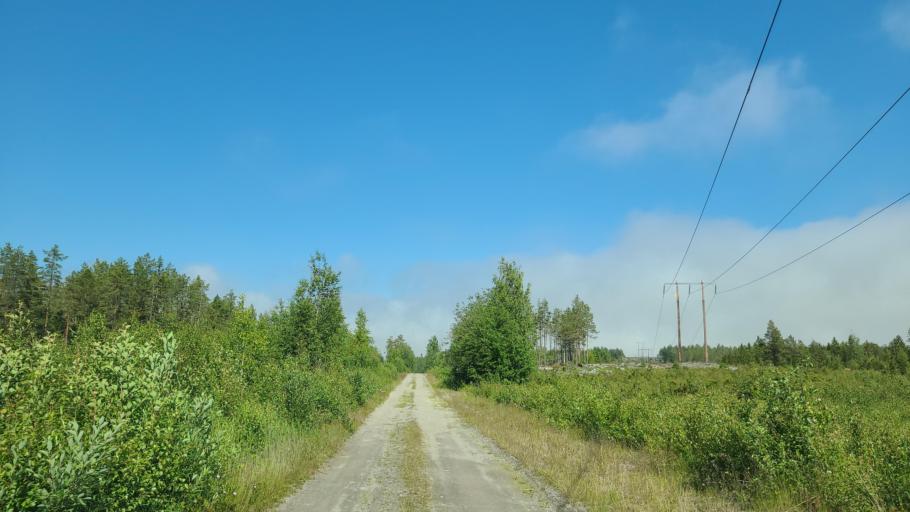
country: SE
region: Vaesternorrland
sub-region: OErnskoeldsviks Kommun
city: Husum
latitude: 63.4414
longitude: 19.2342
